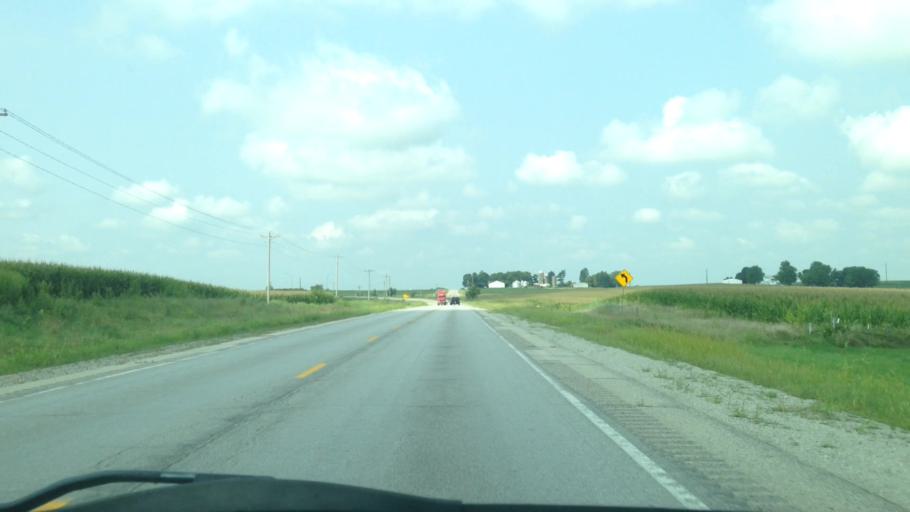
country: US
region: Iowa
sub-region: Benton County
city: Walford
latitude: 41.8762
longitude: -91.8601
